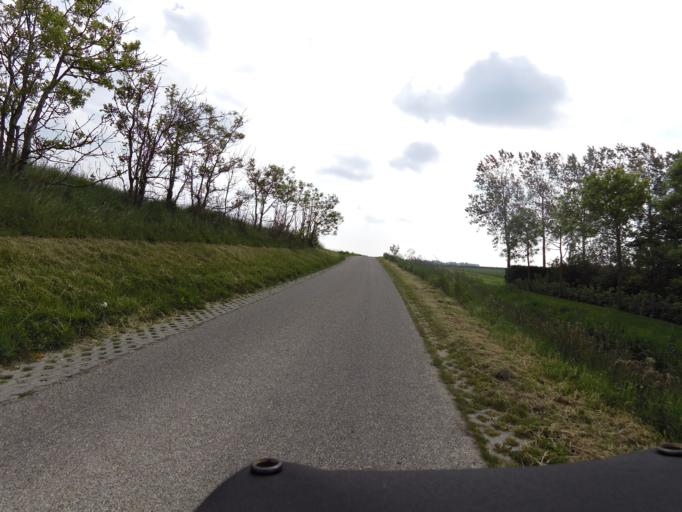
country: NL
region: Zeeland
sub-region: Gemeente Noord-Beveland
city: Kamperland
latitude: 51.5938
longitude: 3.6950
